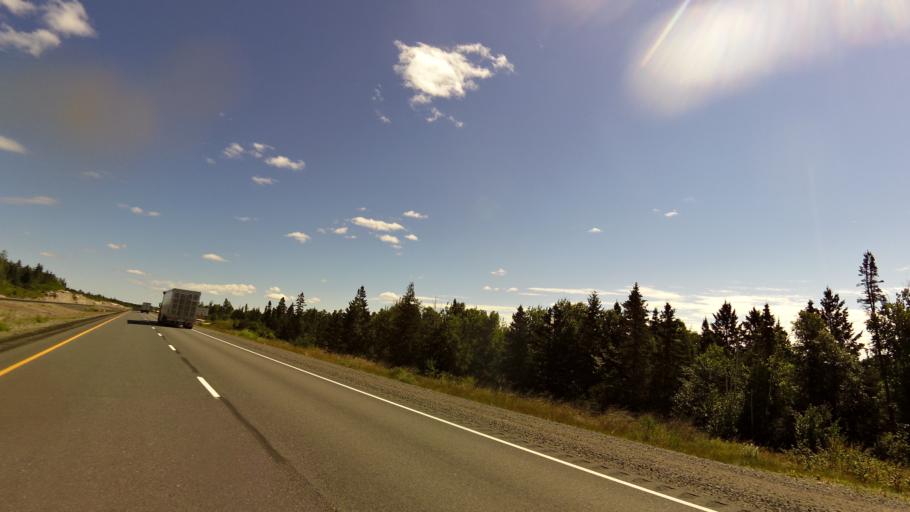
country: CA
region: Ontario
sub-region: Thunder Bay District
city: Thunder Bay
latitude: 48.5473
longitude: -88.9138
